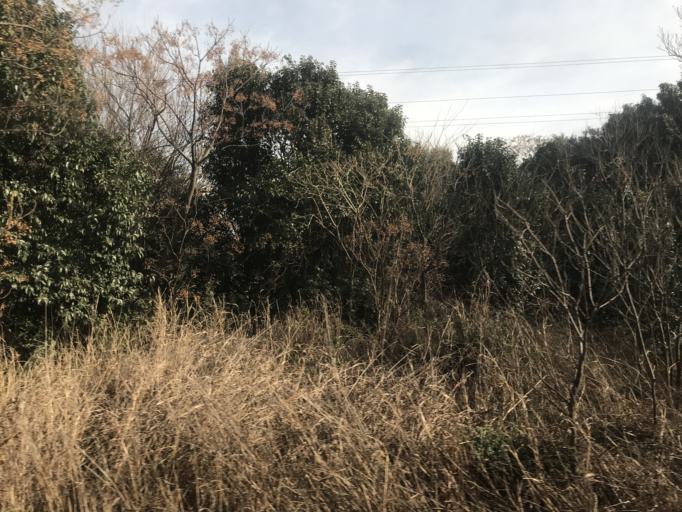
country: AR
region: Cordoba
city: Laguna Larga
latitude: -31.7849
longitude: -63.7962
